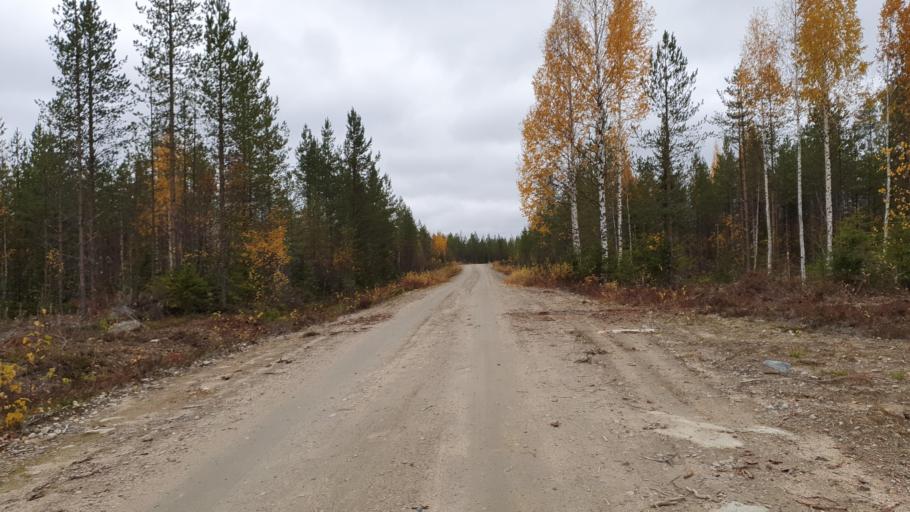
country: FI
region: Kainuu
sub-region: Kehys-Kainuu
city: Kuhmo
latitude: 64.4542
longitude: 29.6070
